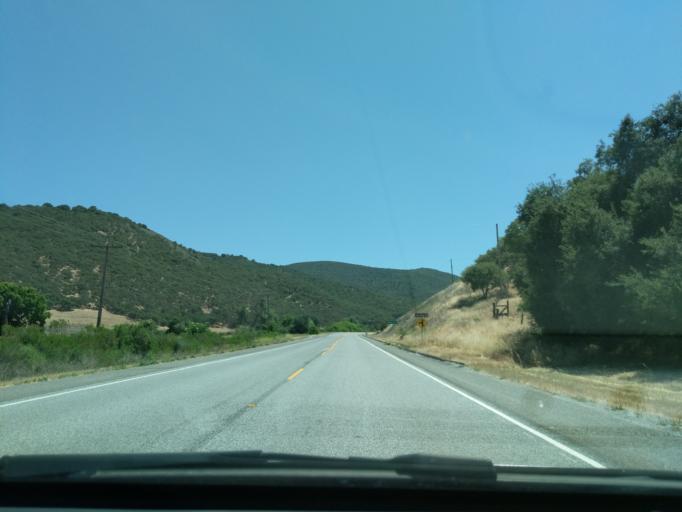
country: US
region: California
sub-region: Monterey County
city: King City
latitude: 36.1161
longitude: -121.1287
